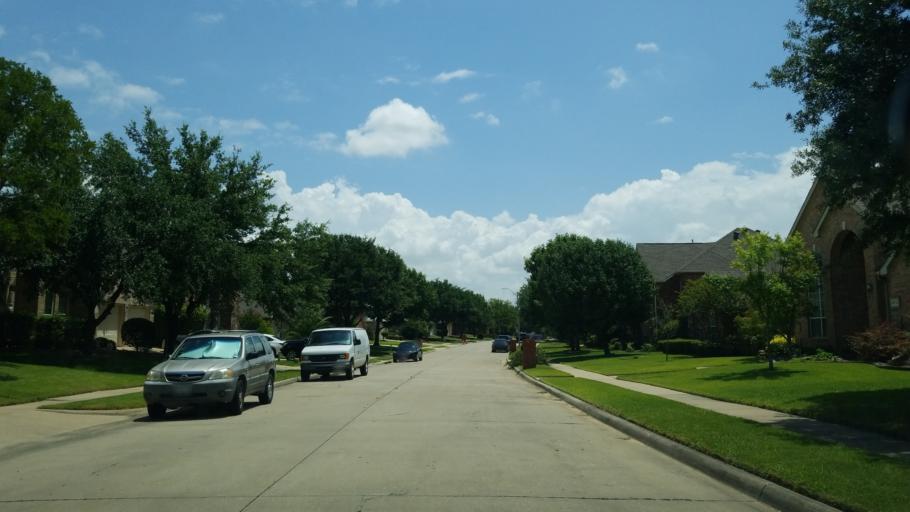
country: US
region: Texas
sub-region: Dallas County
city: Coppell
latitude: 32.9419
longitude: -96.9615
